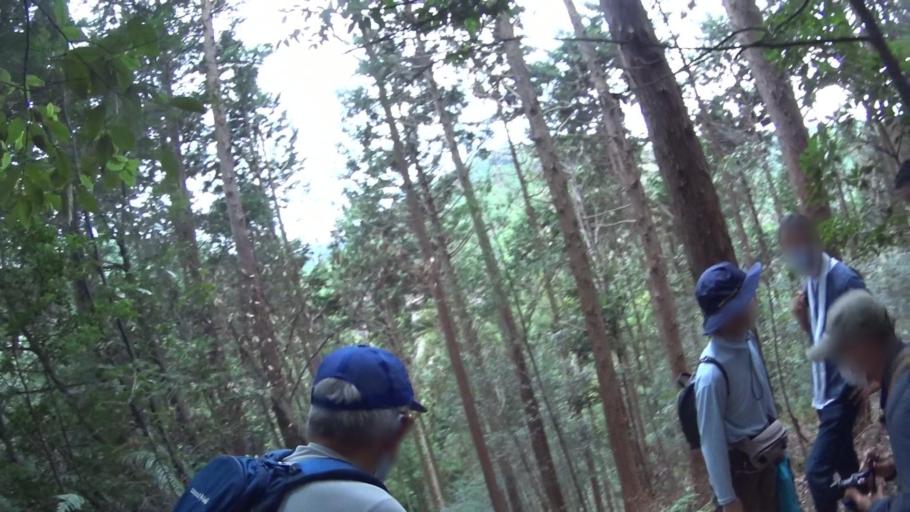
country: JP
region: Gifu
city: Tarui
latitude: 35.2907
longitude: 136.4145
